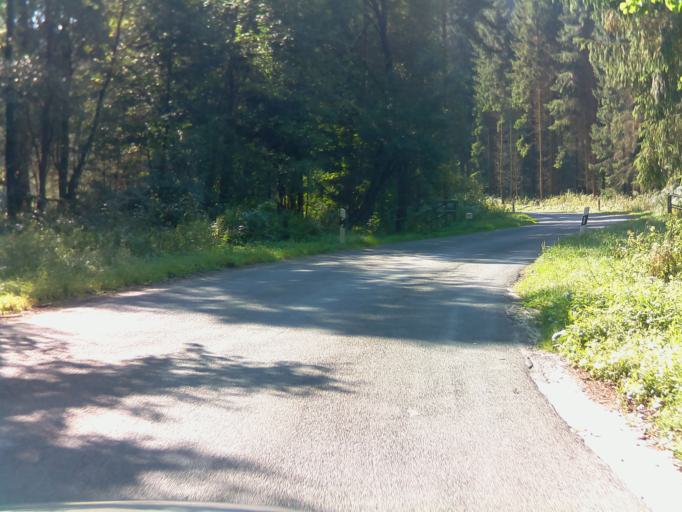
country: DE
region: Thuringia
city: Herschdorf
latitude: 50.7374
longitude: 11.5272
